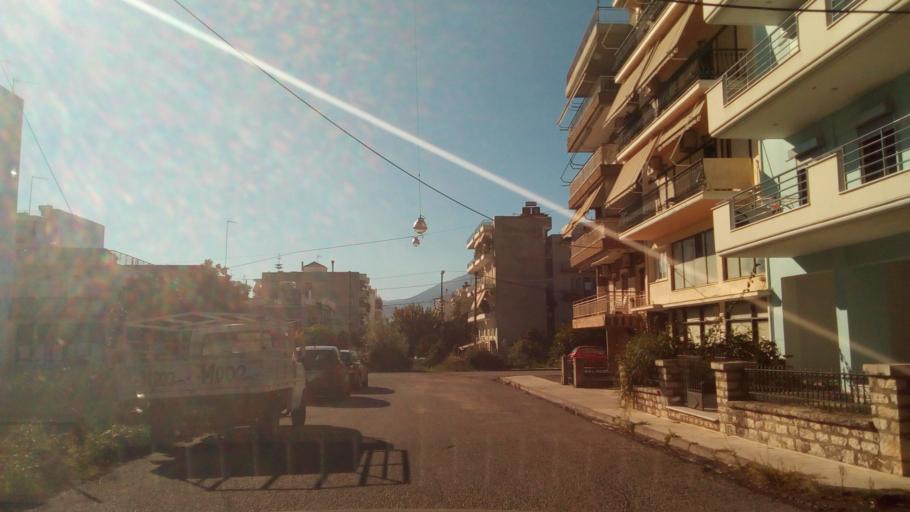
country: GR
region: West Greece
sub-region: Nomos Aitolias kai Akarnanias
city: Nafpaktos
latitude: 38.3915
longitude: 21.8215
